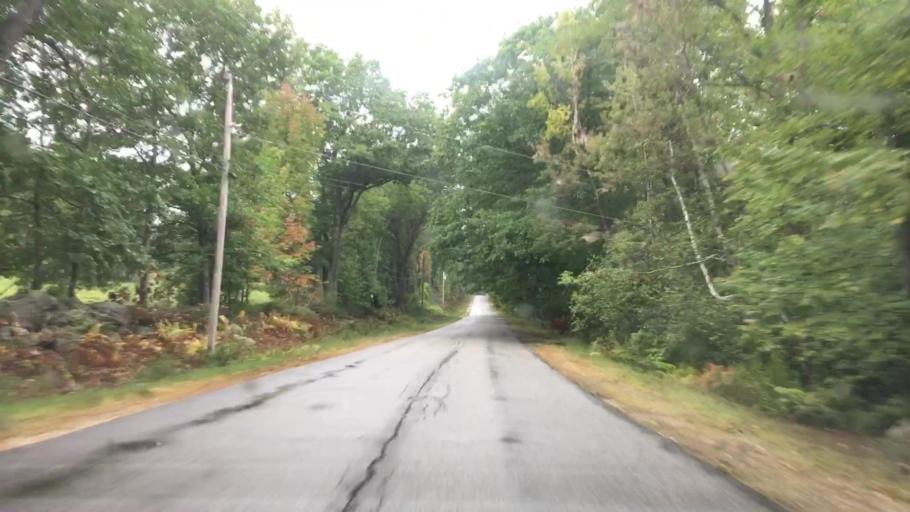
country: US
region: Maine
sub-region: Cumberland County
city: Harrison
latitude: 44.0556
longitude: -70.6196
